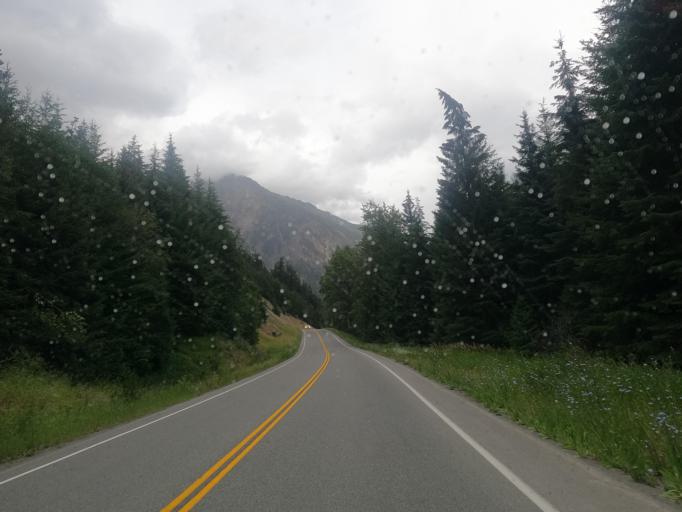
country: CA
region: British Columbia
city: Lillooet
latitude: 50.5191
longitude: -122.1672
